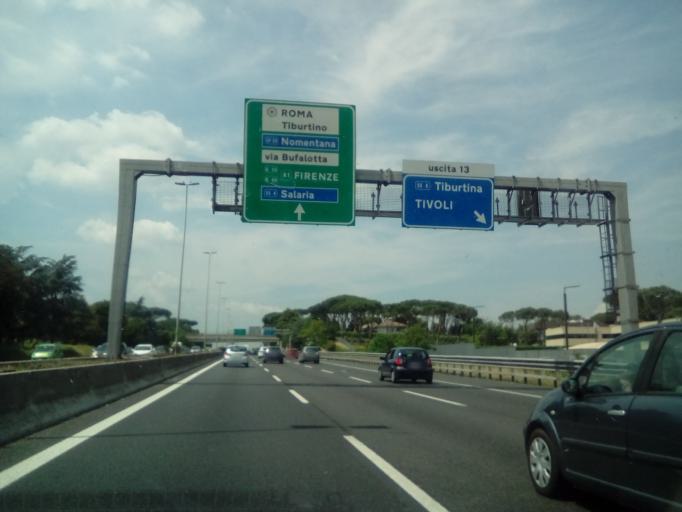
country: IT
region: Latium
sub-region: Citta metropolitana di Roma Capitale
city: Setteville
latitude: 41.9278
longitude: 12.6057
